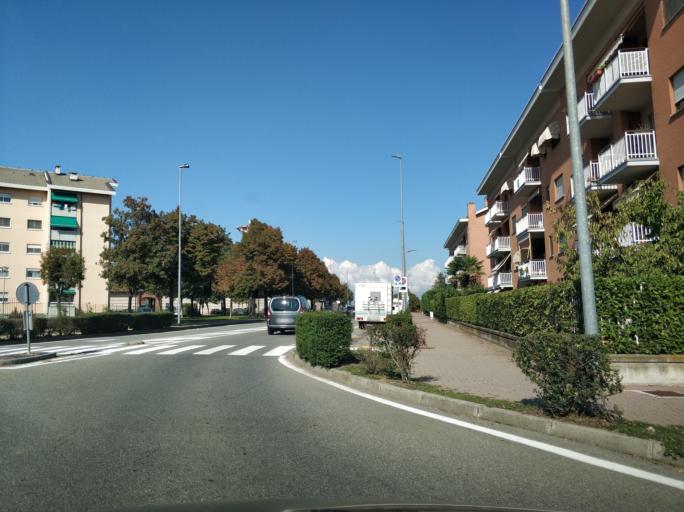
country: IT
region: Piedmont
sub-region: Provincia di Torino
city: Borgaro Torinese
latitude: 45.1568
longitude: 7.6583
